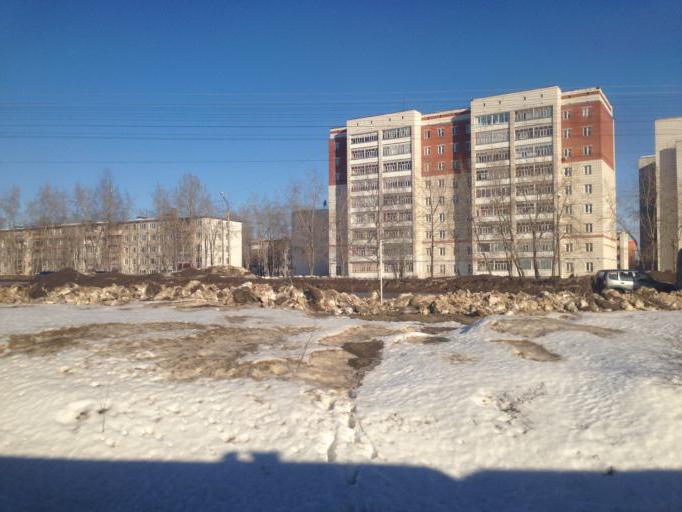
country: RU
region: Komi Republic
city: Ezhva
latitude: 61.7961
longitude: 50.7375
